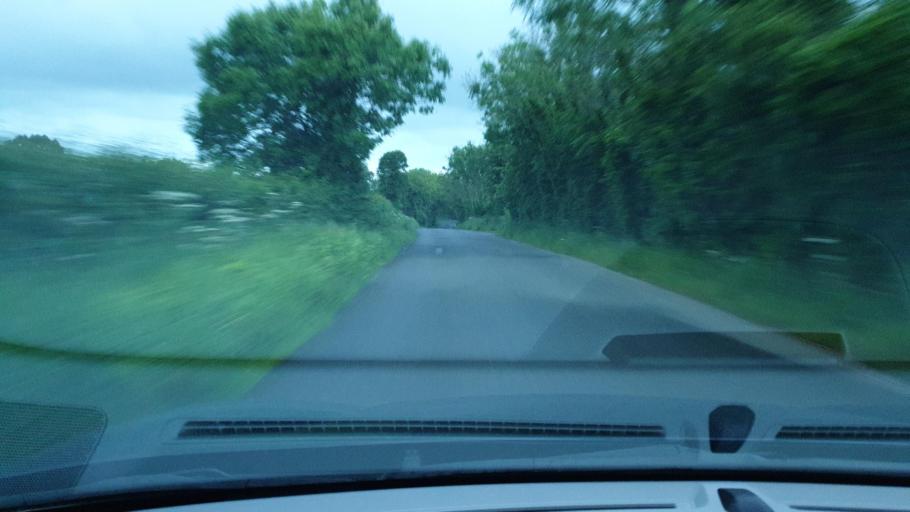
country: IE
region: Leinster
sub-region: An Mhi
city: Ashbourne
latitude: 53.5151
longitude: -6.3457
